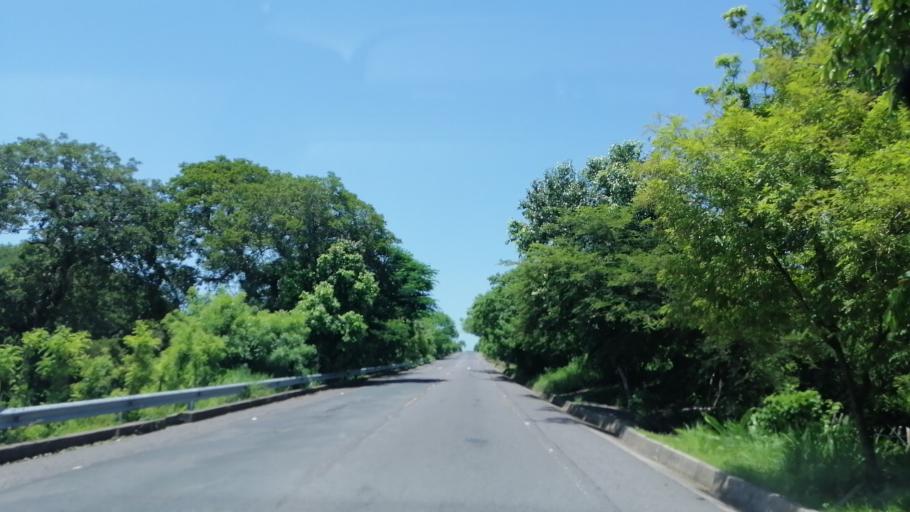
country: SV
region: Chalatenango
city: Chalatenango
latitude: 14.0306
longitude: -88.9514
